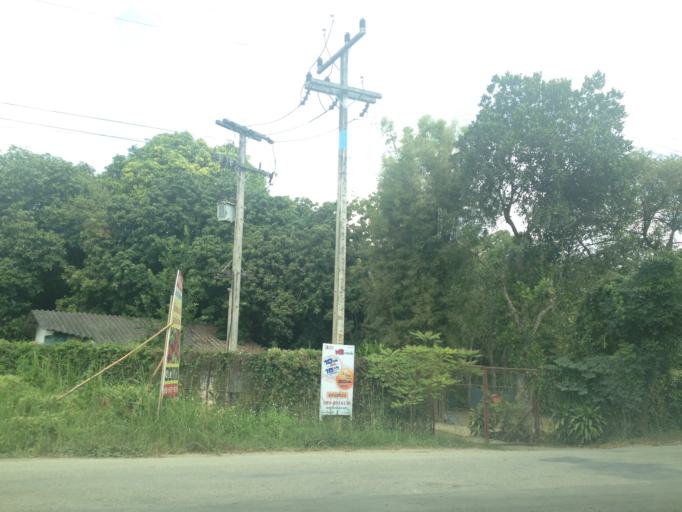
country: TH
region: Chiang Mai
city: Hang Dong
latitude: 18.7326
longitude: 98.8876
